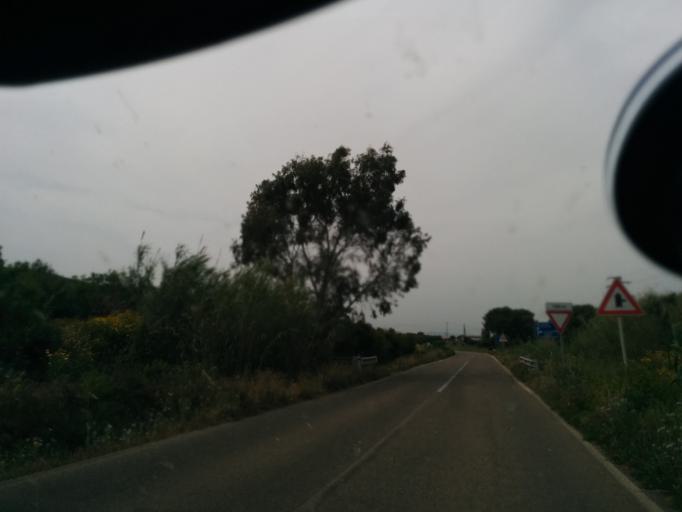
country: IT
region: Sardinia
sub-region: Provincia di Carbonia-Iglesias
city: Sant'Antioco
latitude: 39.0390
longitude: 8.4544
